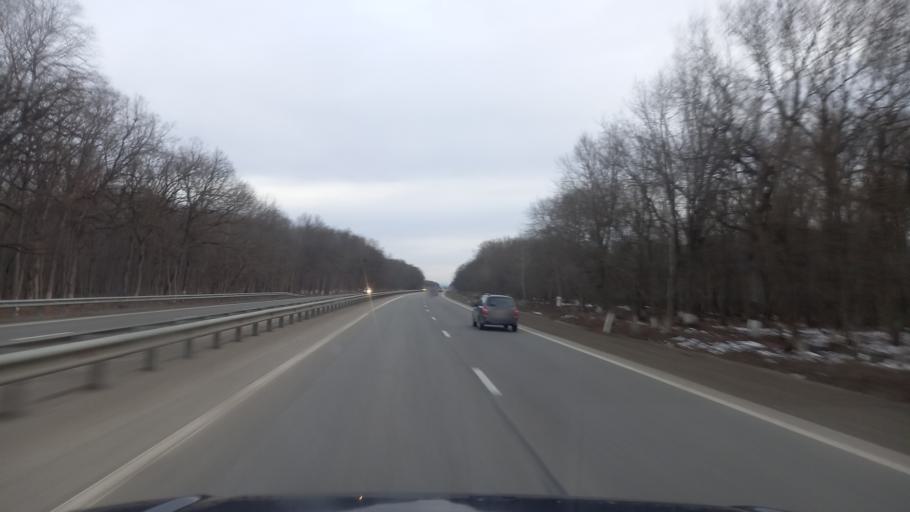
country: RU
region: Adygeya
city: Khanskaya
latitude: 44.7340
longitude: 39.9420
